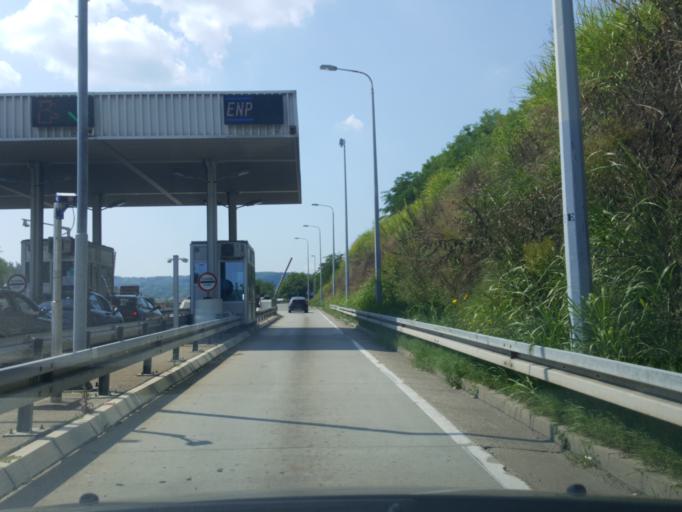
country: RS
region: Central Serbia
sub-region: Belgrade
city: Sopot
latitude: 44.5633
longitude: 20.6694
